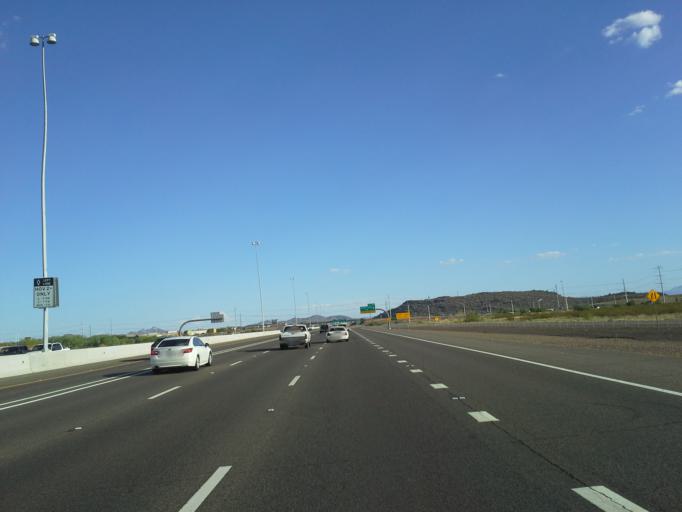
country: US
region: Arizona
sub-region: Maricopa County
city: Anthem
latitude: 33.7196
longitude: -112.1191
